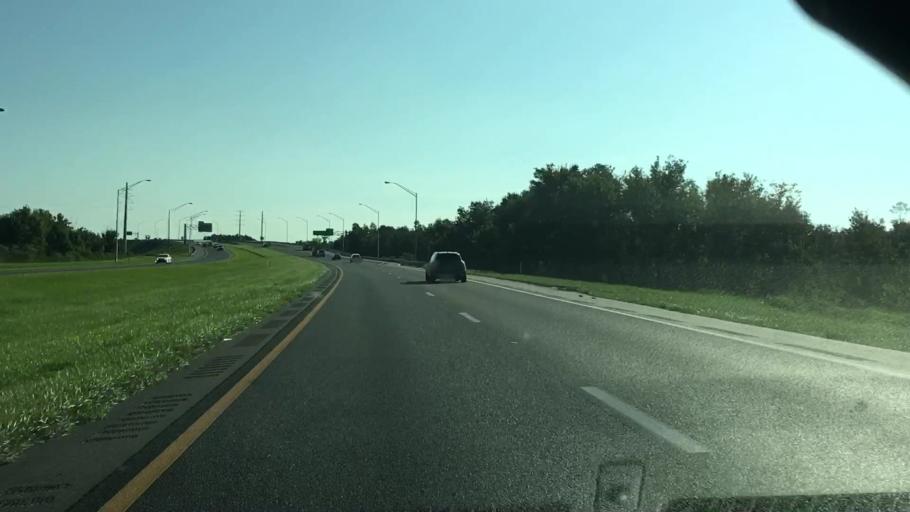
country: US
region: Florida
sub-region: Orange County
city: Taft
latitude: 28.4054
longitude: -81.2351
